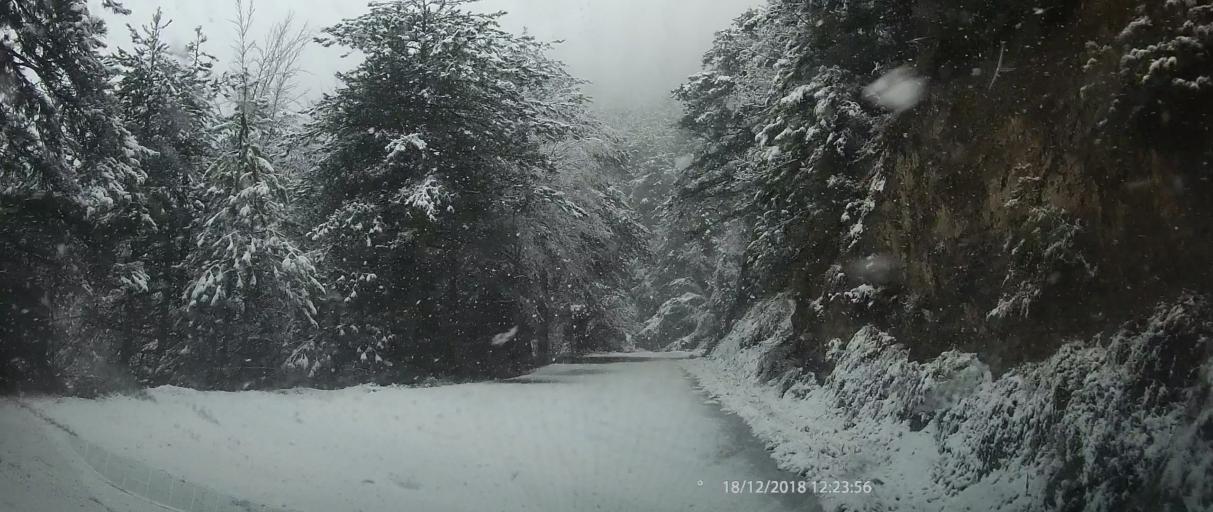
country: GR
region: Central Macedonia
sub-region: Nomos Pierias
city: Litochoro
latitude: 40.0913
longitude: 22.4179
